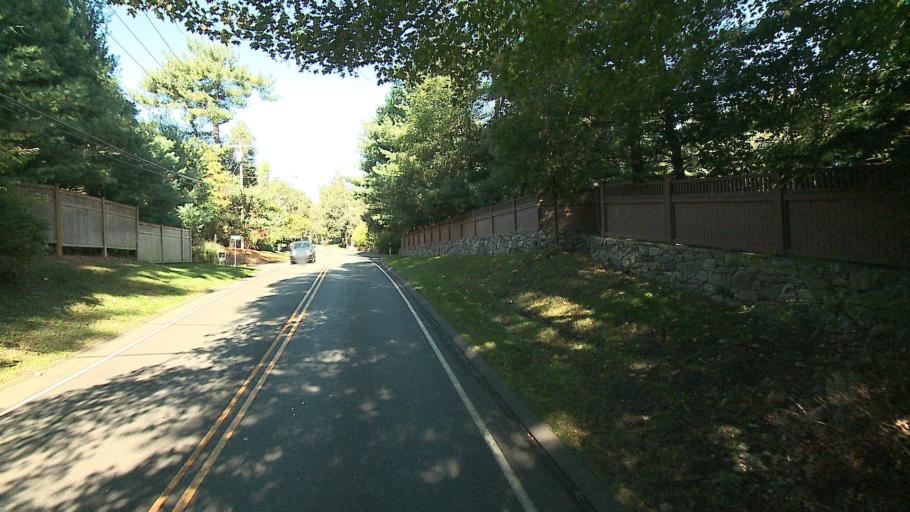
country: US
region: Connecticut
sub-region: Fairfield County
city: Westport
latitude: 41.1500
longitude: -73.3534
